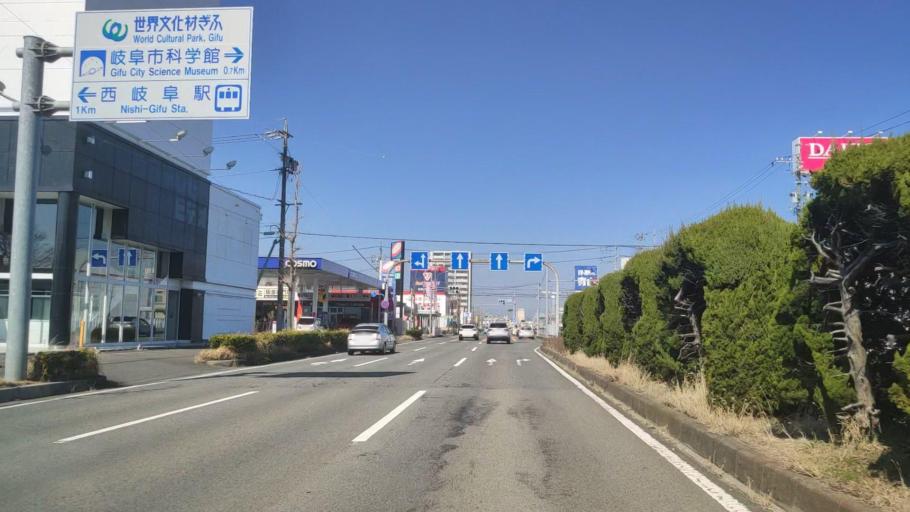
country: JP
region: Gifu
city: Gifu-shi
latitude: 35.4013
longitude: 136.7265
